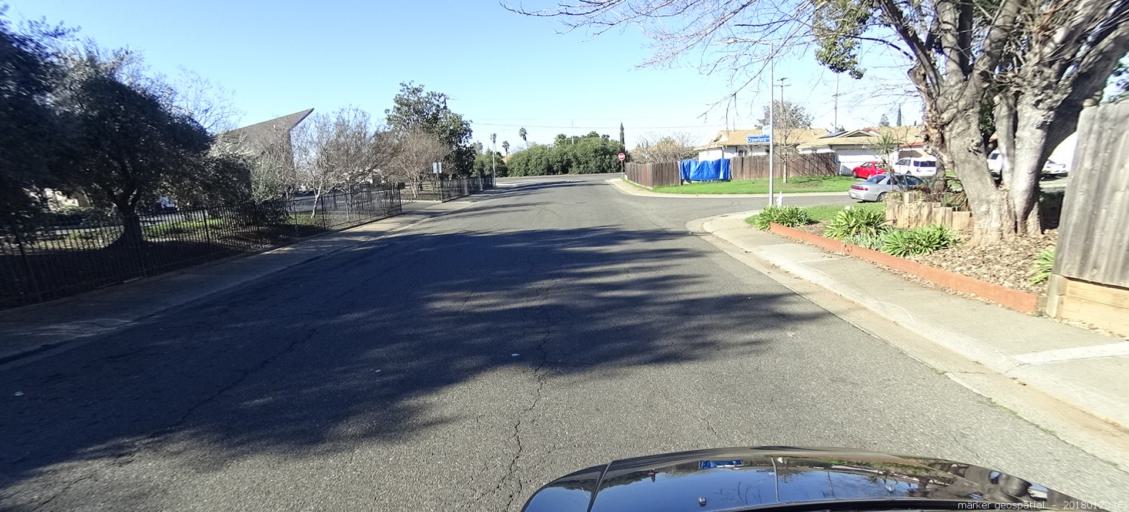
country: US
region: California
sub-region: Sacramento County
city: Rancho Cordova
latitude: 38.5689
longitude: -121.3170
